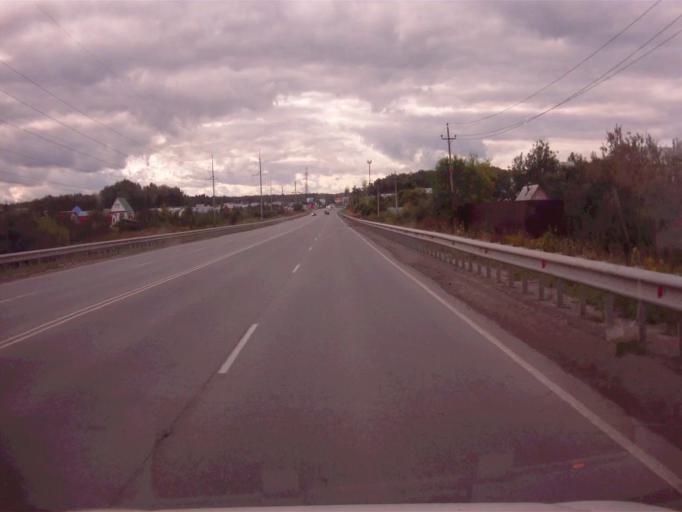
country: RU
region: Chelyabinsk
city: Sargazy
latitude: 55.1409
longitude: 61.2595
